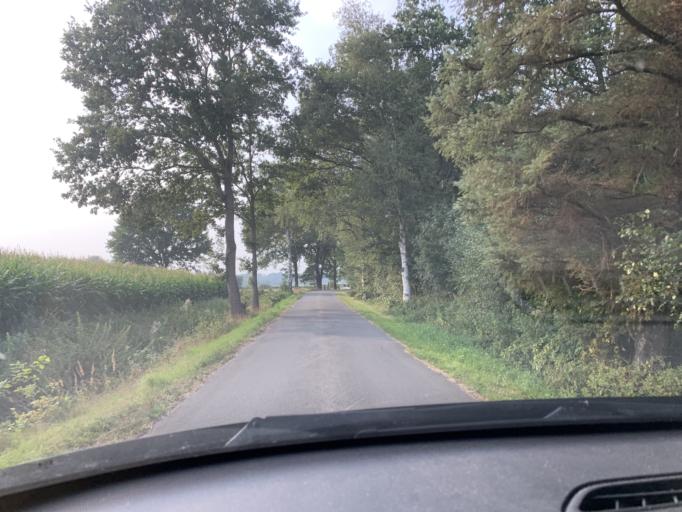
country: DE
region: Lower Saxony
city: Apen
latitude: 53.2439
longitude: 7.8273
